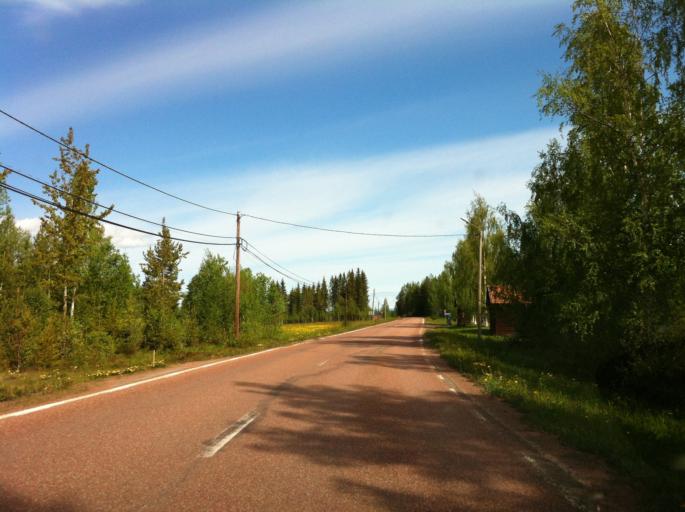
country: SE
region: Dalarna
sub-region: Mora Kommun
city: Mora
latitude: 60.8762
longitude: 14.5769
